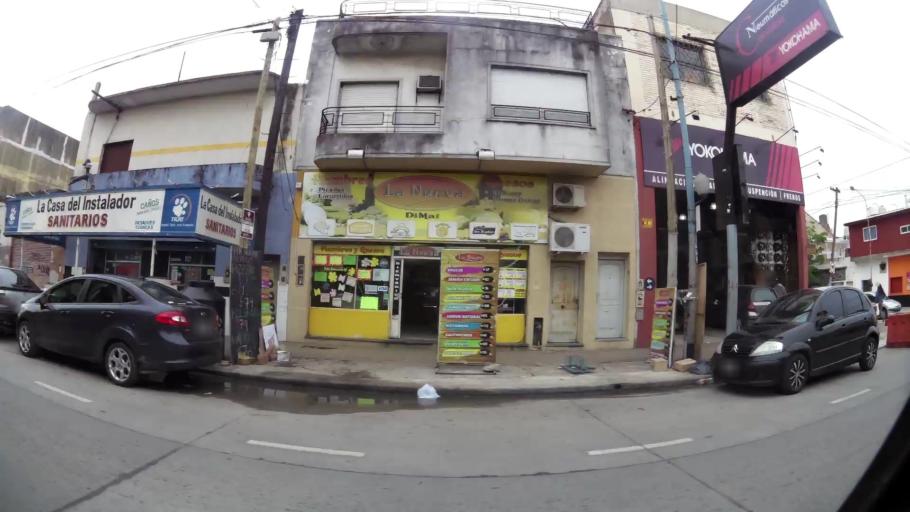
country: AR
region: Buenos Aires
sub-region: Partido de Lanus
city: Lanus
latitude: -34.7272
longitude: -58.3551
